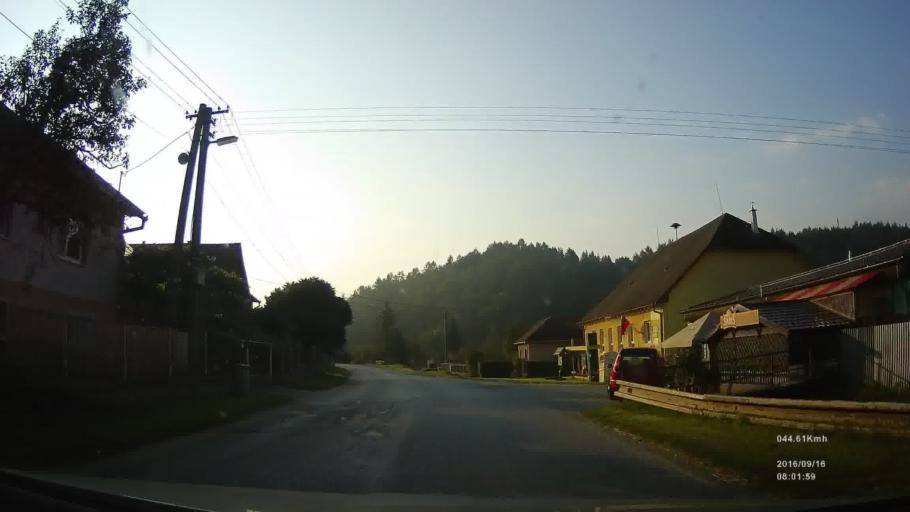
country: SK
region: Presovsky
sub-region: Okres Presov
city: Presov
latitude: 48.9114
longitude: 21.1765
